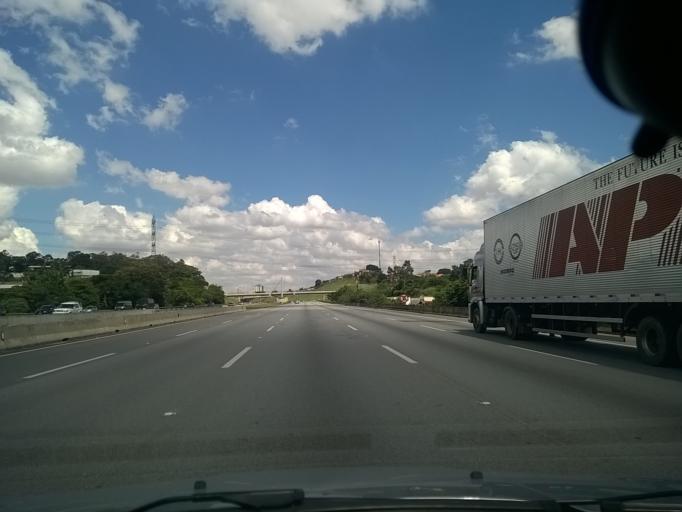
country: BR
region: Sao Paulo
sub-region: Osasco
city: Osasco
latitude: -23.4692
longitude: -46.7496
